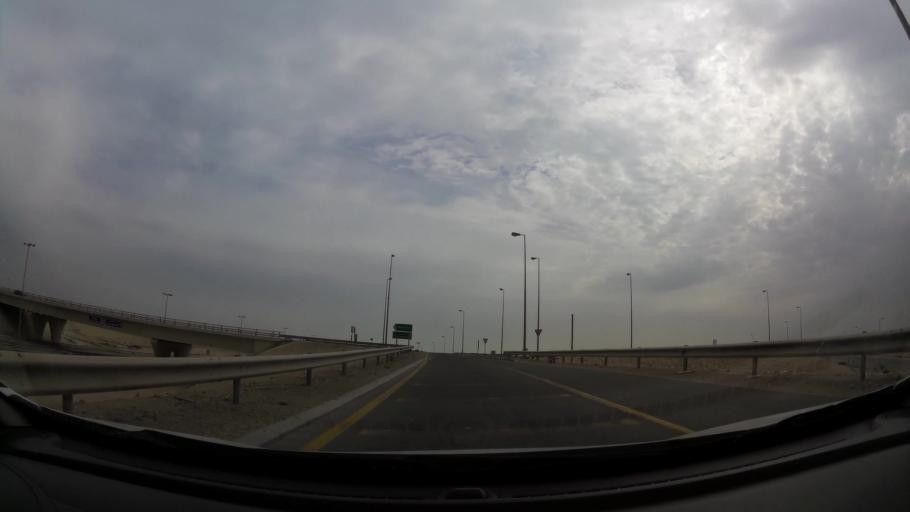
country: BH
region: Northern
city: Ar Rifa'
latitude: 26.0485
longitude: 50.6066
